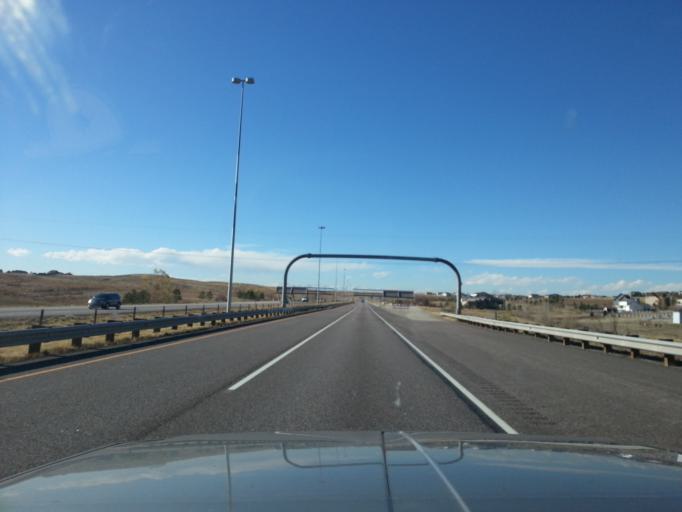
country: US
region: Colorado
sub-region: Adams County
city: Todd Creek
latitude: 39.9527
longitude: -104.8694
